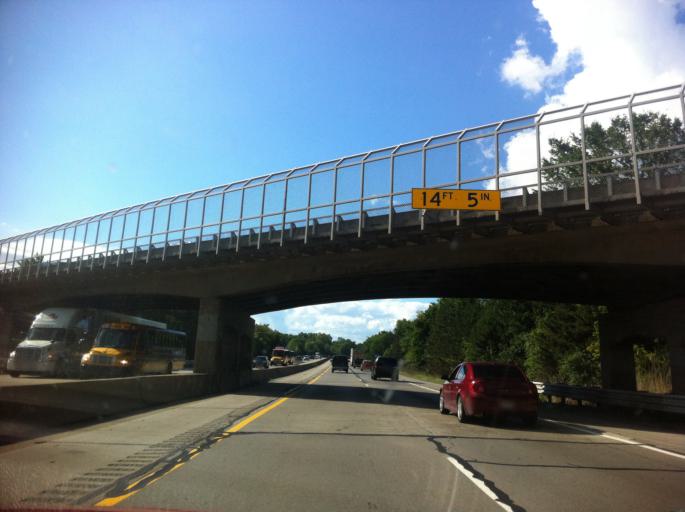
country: US
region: Michigan
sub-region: Washtenaw County
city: Ann Arbor
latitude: 42.2464
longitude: -83.7645
